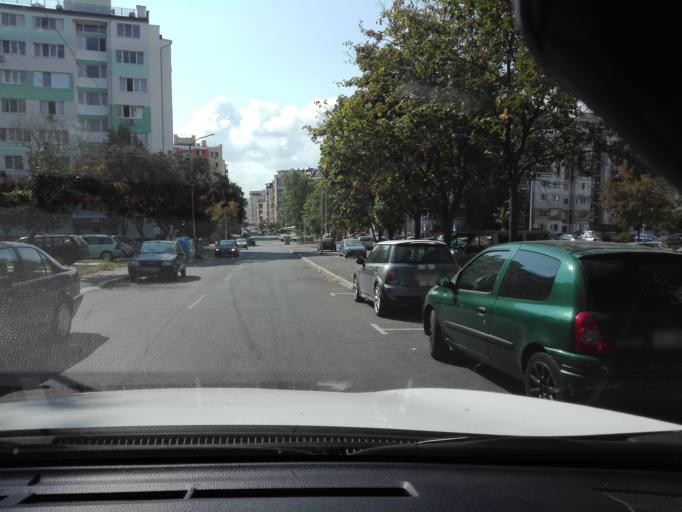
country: BG
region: Burgas
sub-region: Obshtina Burgas
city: Burgas
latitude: 42.4549
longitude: 27.4217
